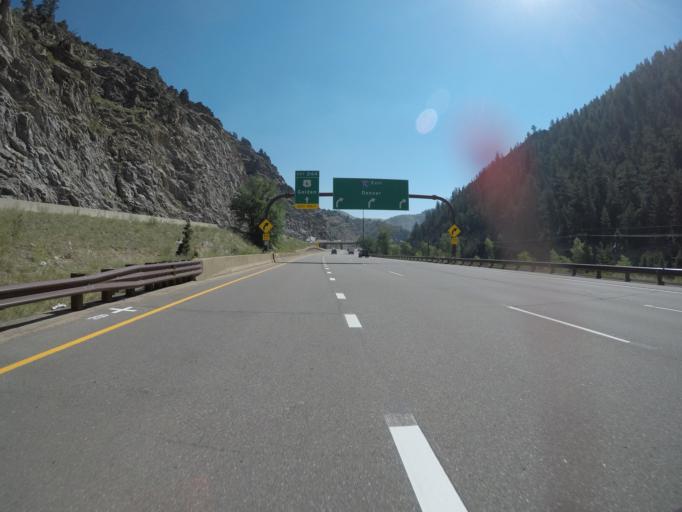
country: US
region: Colorado
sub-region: Clear Creek County
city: Idaho Springs
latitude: 39.7444
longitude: -105.4417
